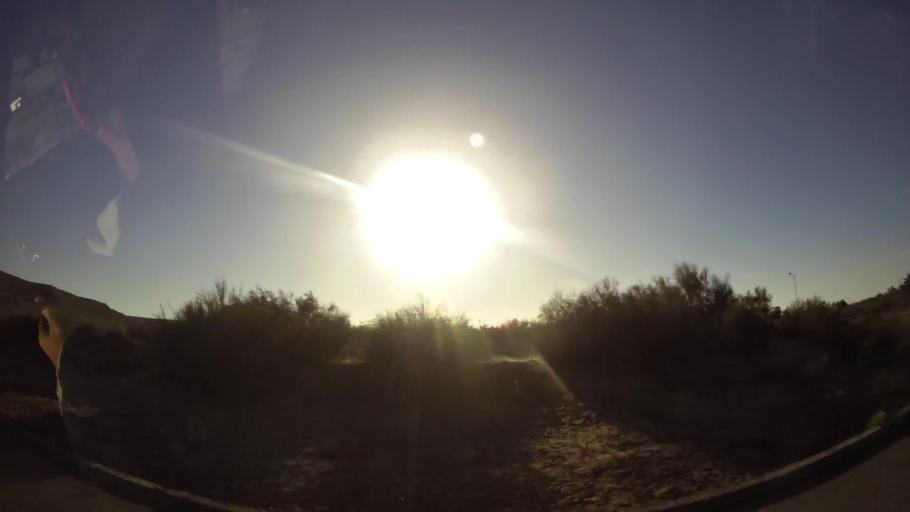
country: MA
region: Oriental
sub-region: Berkane-Taourirt
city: Madagh
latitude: 35.0778
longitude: -2.2467
